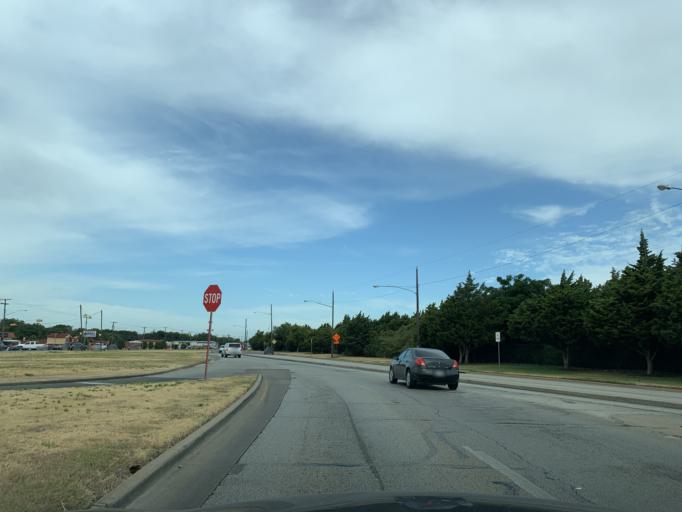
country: US
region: Texas
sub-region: Dallas County
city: Cockrell Hill
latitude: 32.7501
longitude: -96.8794
